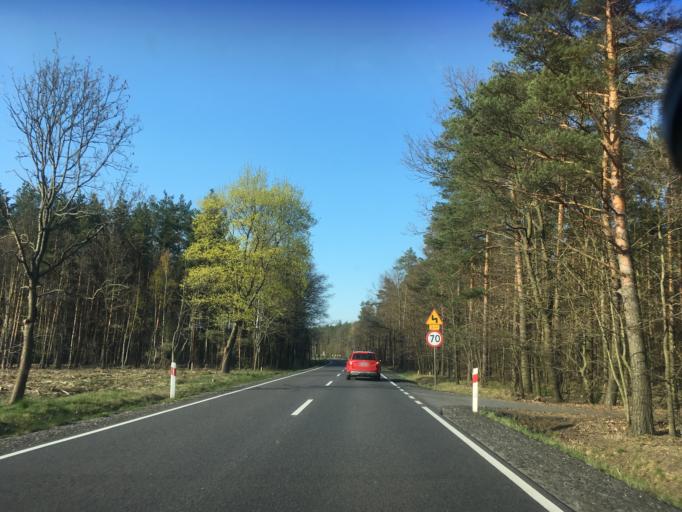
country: PL
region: Lubusz
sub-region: Powiat zaganski
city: Szprotawa
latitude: 51.4947
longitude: 15.6235
